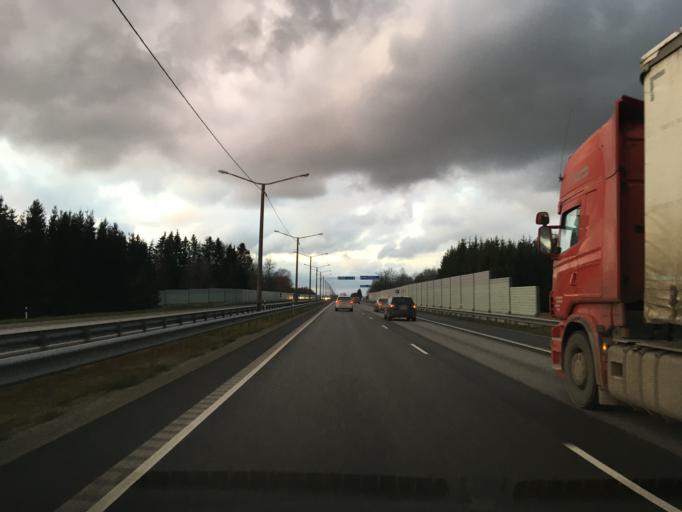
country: EE
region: Harju
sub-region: Rae vald
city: Jueri
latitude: 59.3731
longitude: 24.8520
